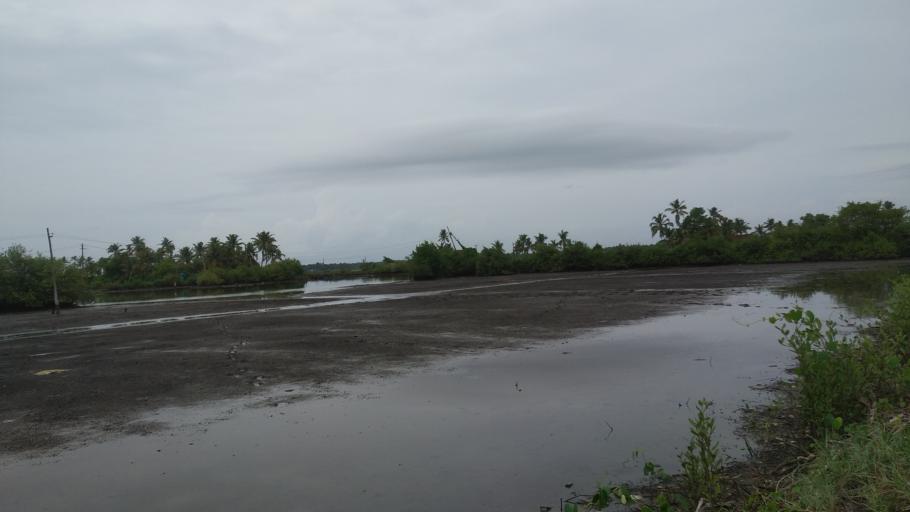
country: IN
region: Kerala
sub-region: Ernakulam
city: Elur
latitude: 10.0807
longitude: 76.2225
